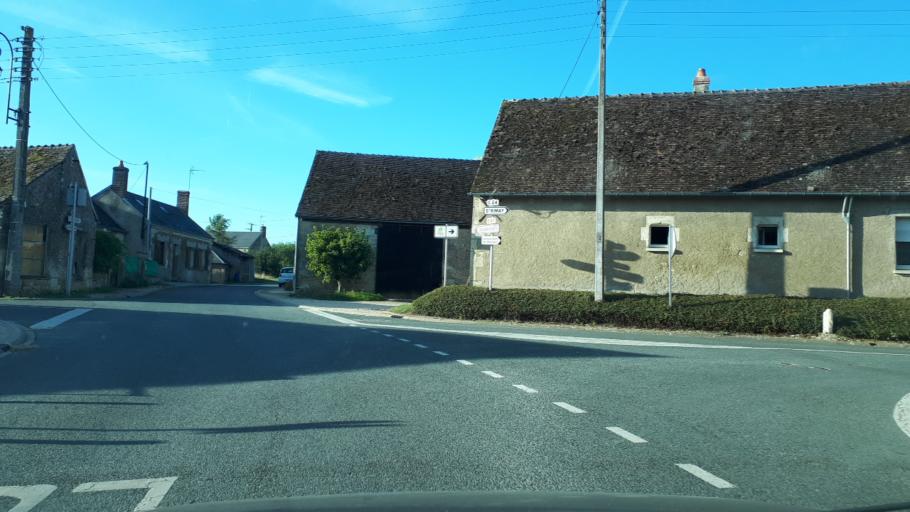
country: FR
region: Centre
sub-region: Departement du Loir-et-Cher
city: Lunay
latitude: 47.7505
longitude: 0.9374
